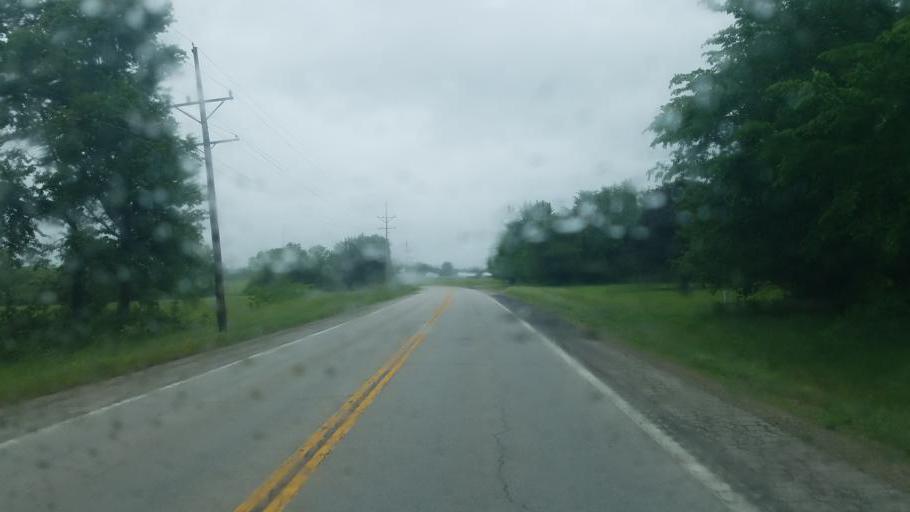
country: US
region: Missouri
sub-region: Carroll County
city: Carrollton
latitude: 39.4180
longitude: -93.4764
